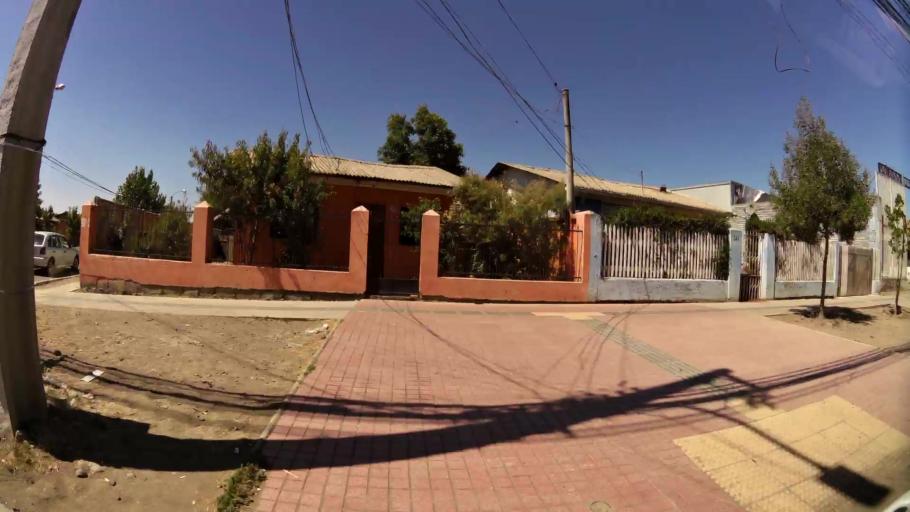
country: CL
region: O'Higgins
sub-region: Provincia de Colchagua
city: Chimbarongo
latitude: -34.5765
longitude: -70.9896
